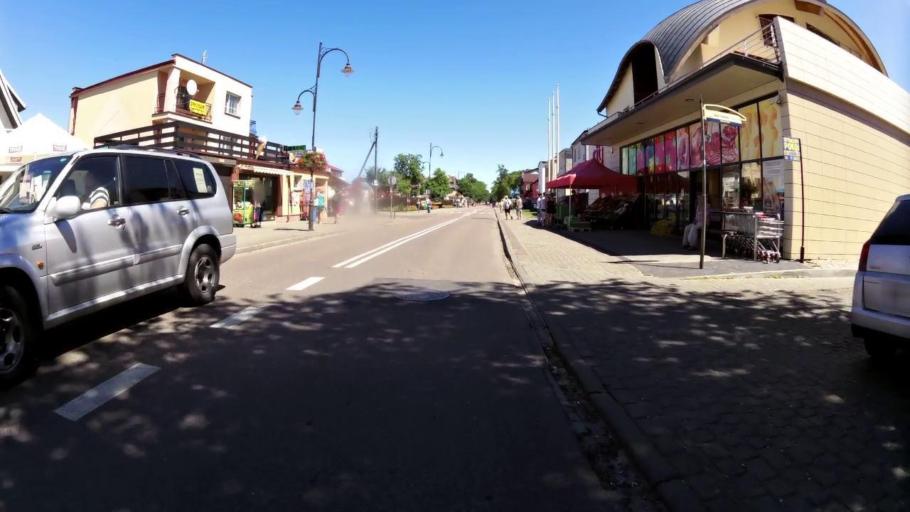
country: PL
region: West Pomeranian Voivodeship
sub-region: Powiat gryficki
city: Mrzezyno
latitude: 54.1440
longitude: 15.2910
